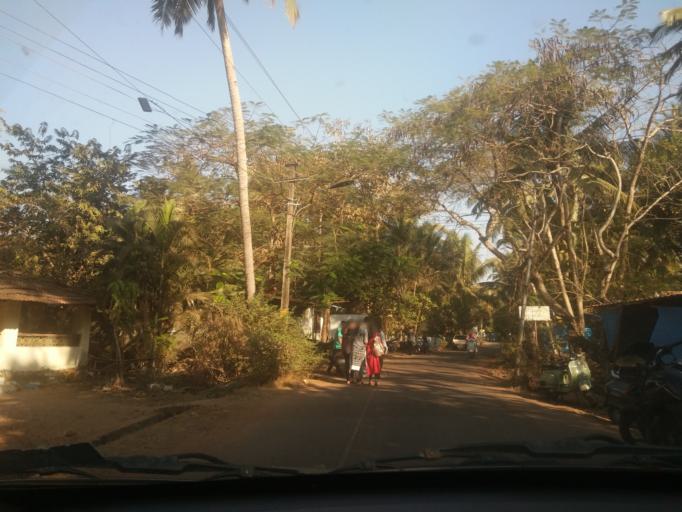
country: IN
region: Goa
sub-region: South Goa
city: Colva
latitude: 15.3070
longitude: 73.9121
